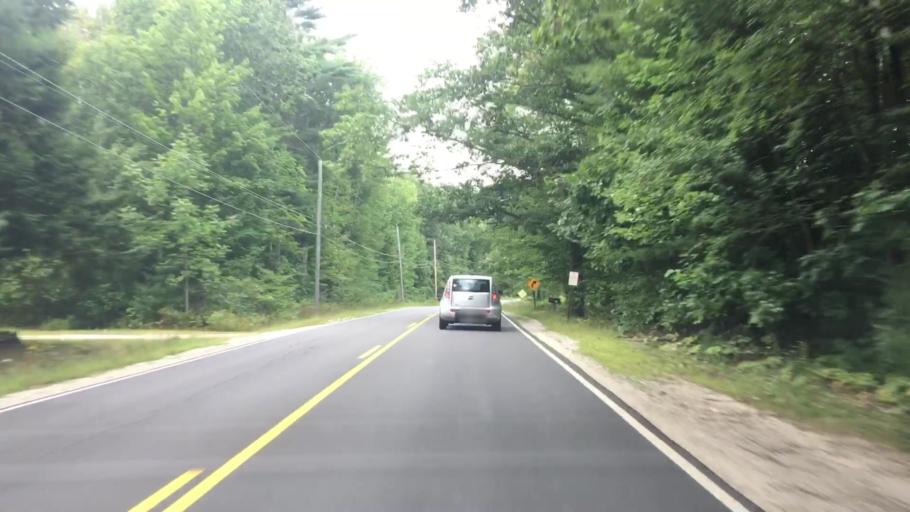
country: US
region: Maine
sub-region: Cumberland County
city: New Gloucester
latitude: 43.8863
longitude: -70.2518
